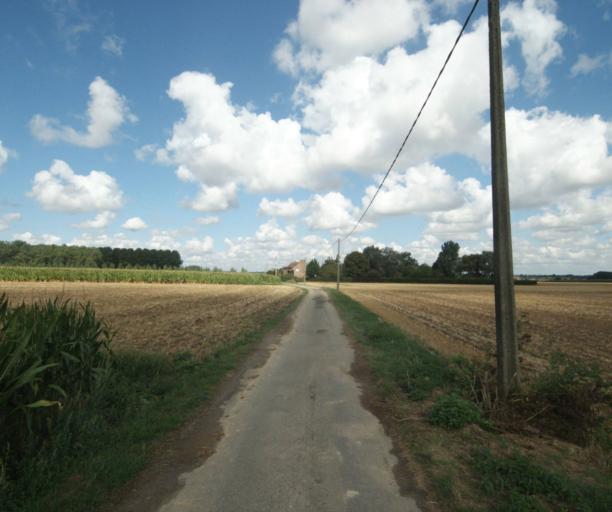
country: FR
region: Nord-Pas-de-Calais
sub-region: Departement du Nord
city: Willems
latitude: 50.6386
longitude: 3.2478
